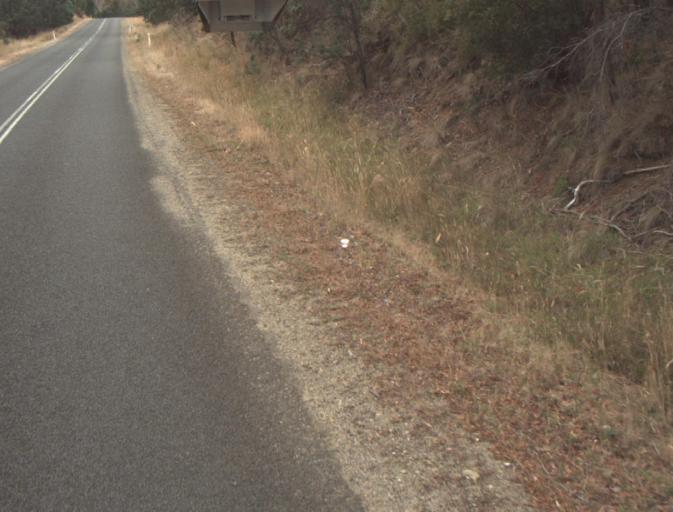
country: AU
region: Tasmania
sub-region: Northern Midlands
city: Evandale
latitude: -41.5048
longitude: 147.3804
